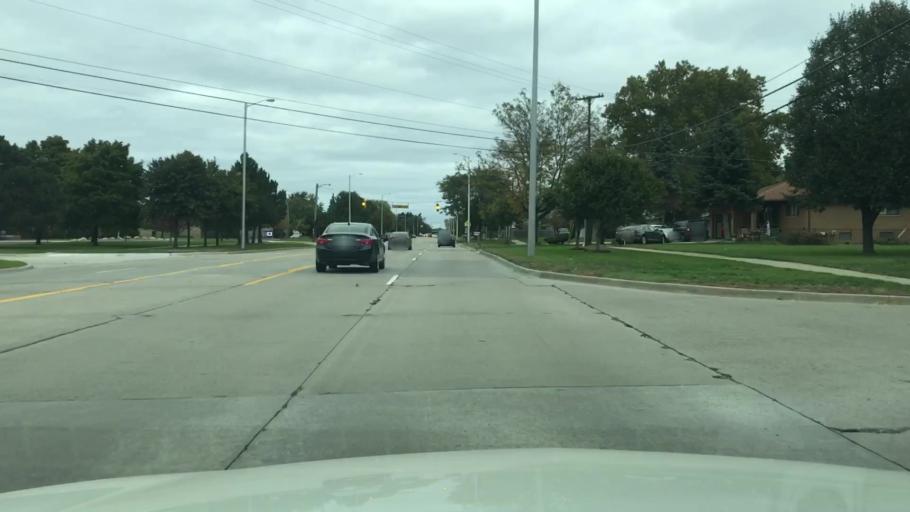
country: US
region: Michigan
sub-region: Macomb County
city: Sterling Heights
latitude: 42.5540
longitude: -83.0694
